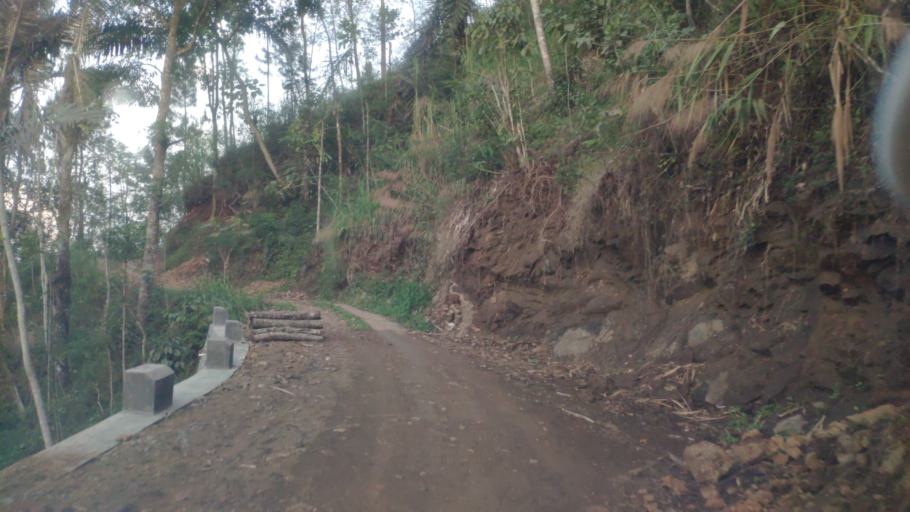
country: ID
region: Central Java
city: Buaran
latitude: -7.2625
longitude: 109.5756
